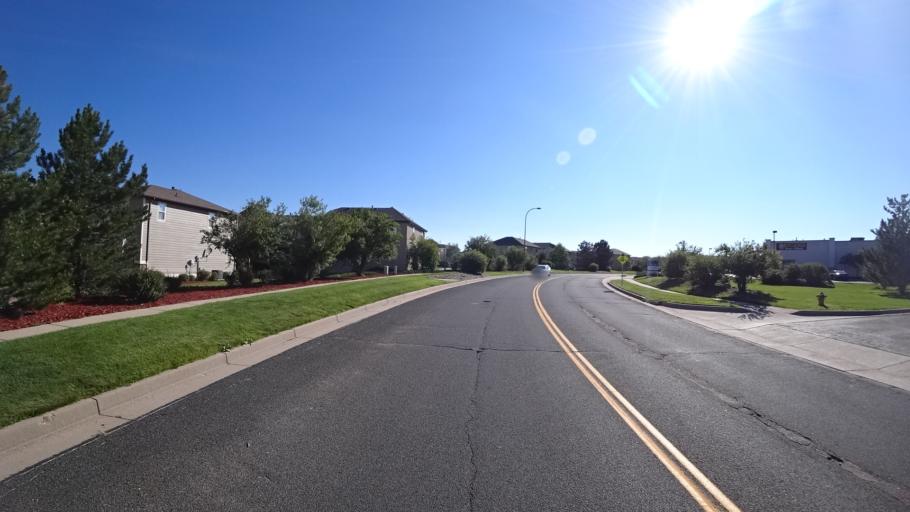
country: US
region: Colorado
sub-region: El Paso County
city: Gleneagle
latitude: 38.9979
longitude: -104.7951
